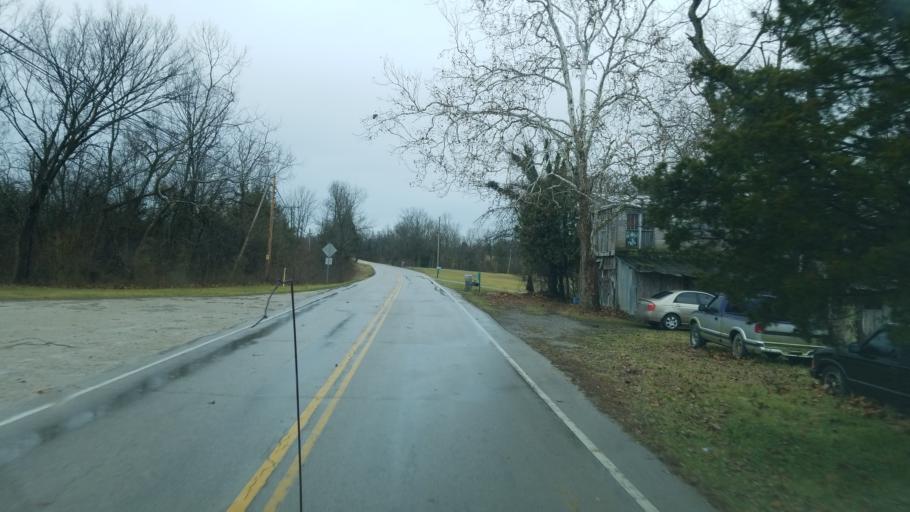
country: US
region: Kentucky
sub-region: Mason County
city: Maysville
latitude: 38.5979
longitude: -83.6722
